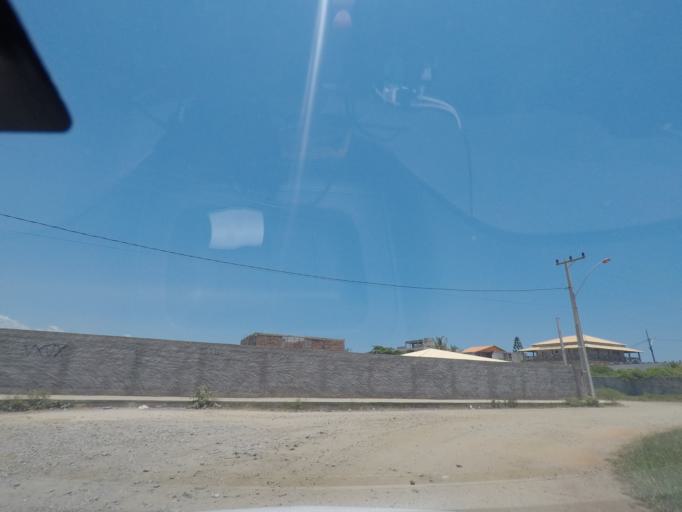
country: BR
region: Rio de Janeiro
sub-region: Niteroi
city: Niteroi
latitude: -22.9680
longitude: -42.9880
